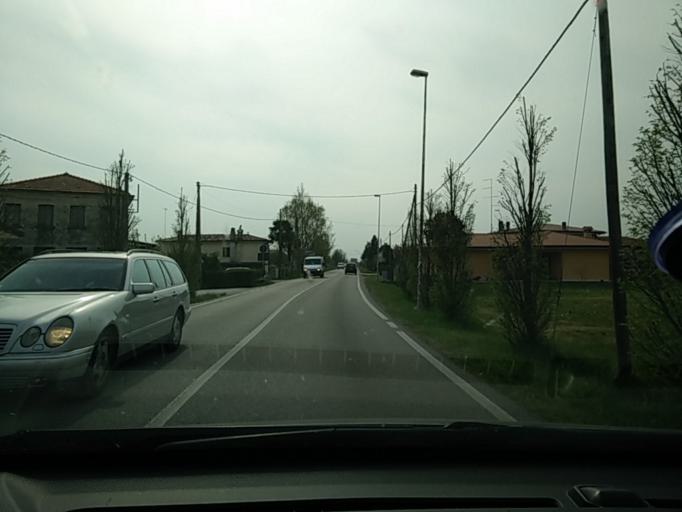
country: IT
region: Veneto
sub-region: Provincia di Treviso
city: Fontanelle
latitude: 45.8298
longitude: 12.4625
